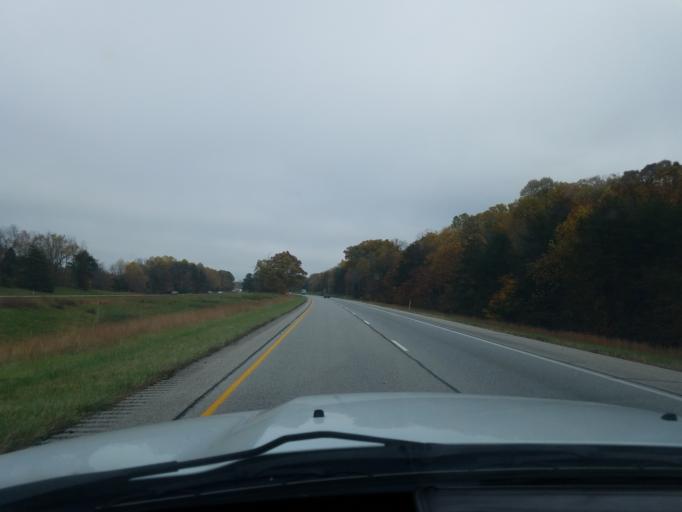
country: US
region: Indiana
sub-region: Floyd County
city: Georgetown
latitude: 38.2545
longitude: -86.0247
